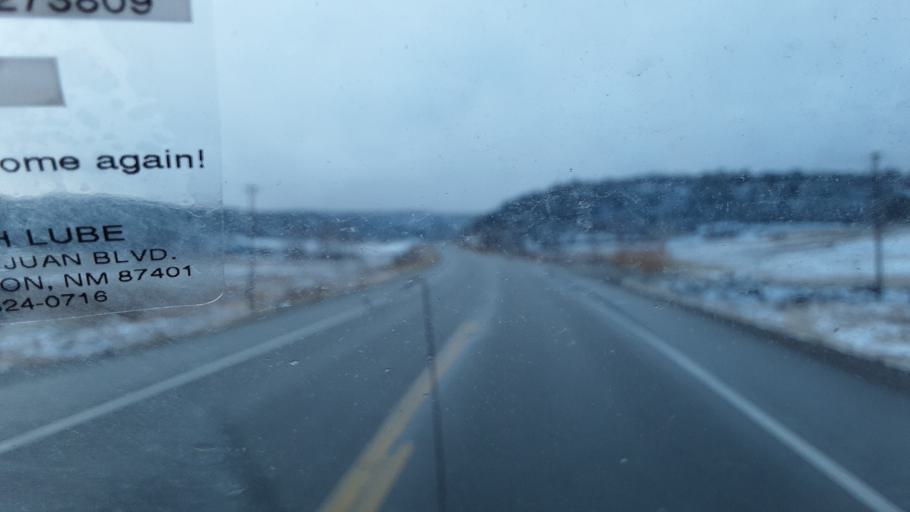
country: US
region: Colorado
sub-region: La Plata County
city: Bayfield
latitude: 37.2258
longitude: -107.6644
